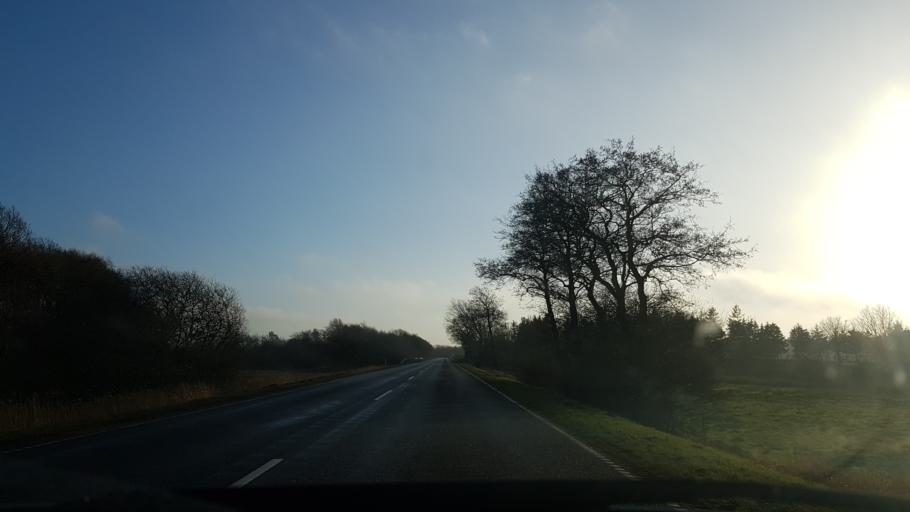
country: DK
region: South Denmark
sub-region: Haderslev Kommune
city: Vojens
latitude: 55.2042
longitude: 9.1927
